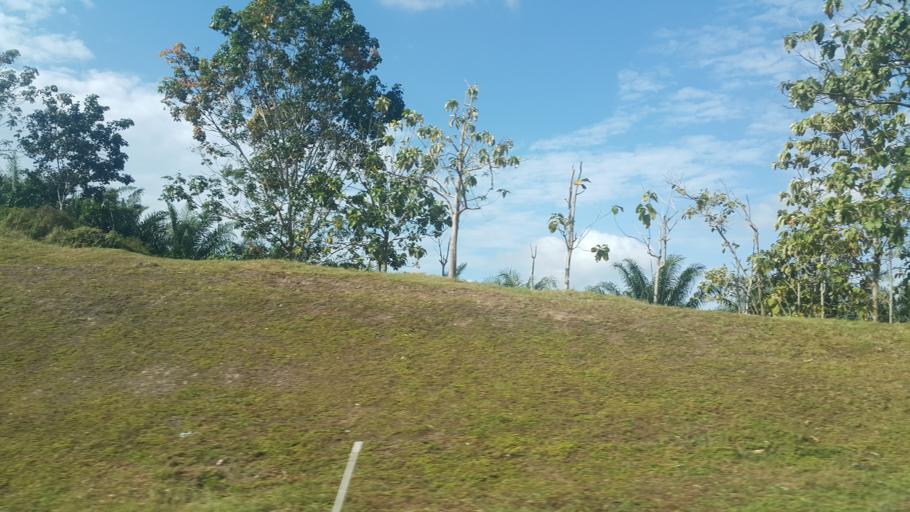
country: MY
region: Johor
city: Kelapa Sawit
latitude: 1.6703
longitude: 103.4890
